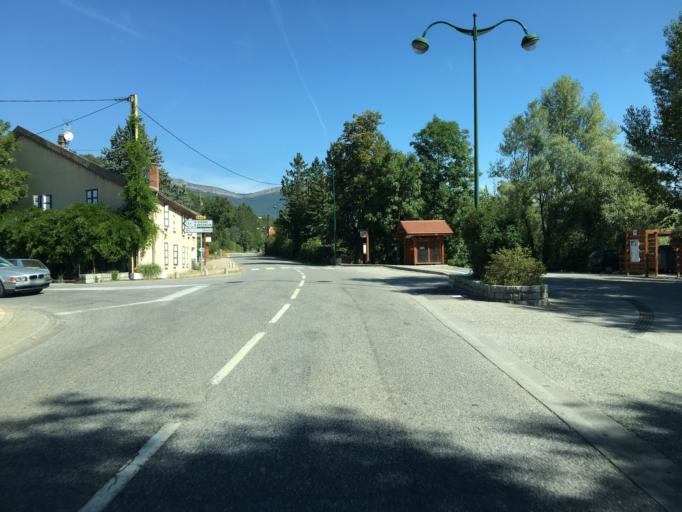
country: FR
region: Provence-Alpes-Cote d'Azur
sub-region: Departement des Hautes-Alpes
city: Serres
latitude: 44.4934
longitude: 5.7287
